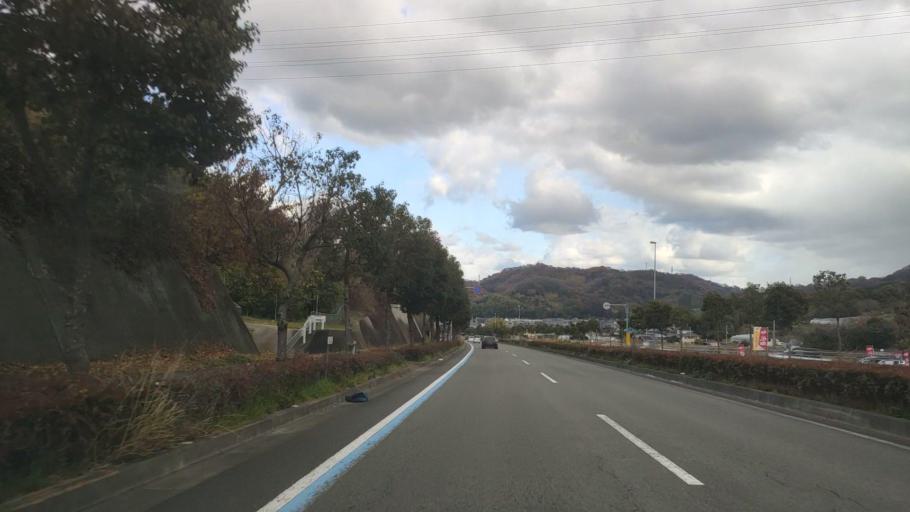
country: JP
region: Ehime
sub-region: Shikoku-chuo Shi
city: Matsuyama
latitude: 33.8926
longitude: 132.7577
